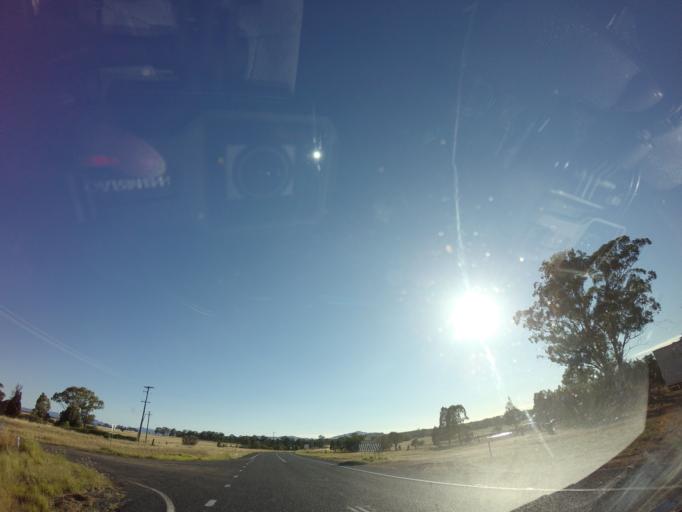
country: AU
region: New South Wales
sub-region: Gilgandra
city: Gilgandra
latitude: -31.5615
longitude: 148.7996
